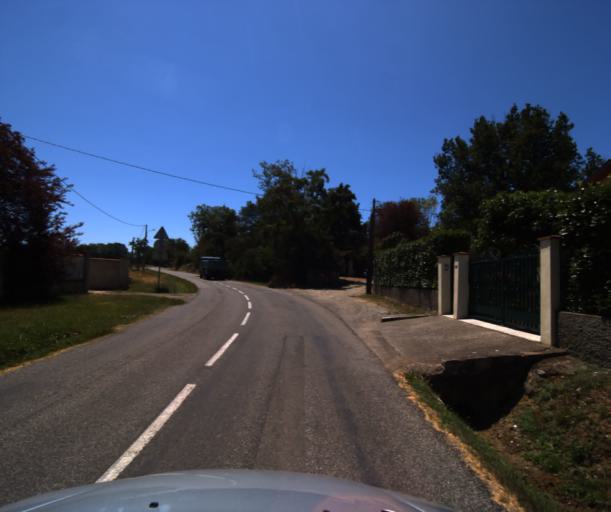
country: FR
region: Midi-Pyrenees
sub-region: Departement de la Haute-Garonne
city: Saubens
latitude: 43.4744
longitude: 1.3522
